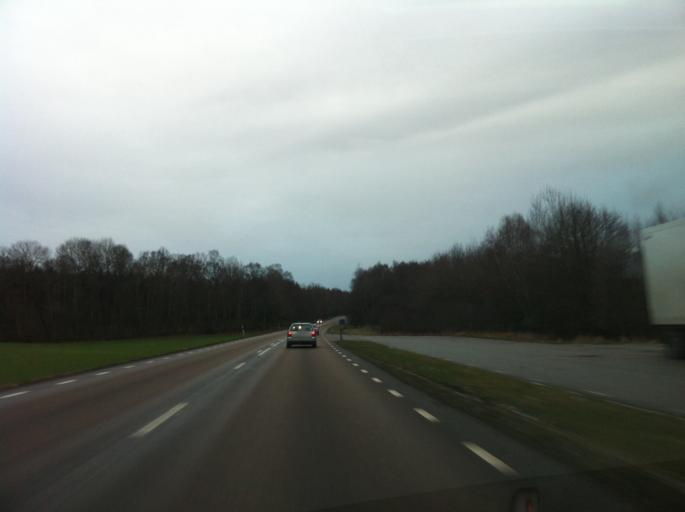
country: SE
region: Skane
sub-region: Bjuvs Kommun
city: Billesholm
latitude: 56.0420
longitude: 12.9692
